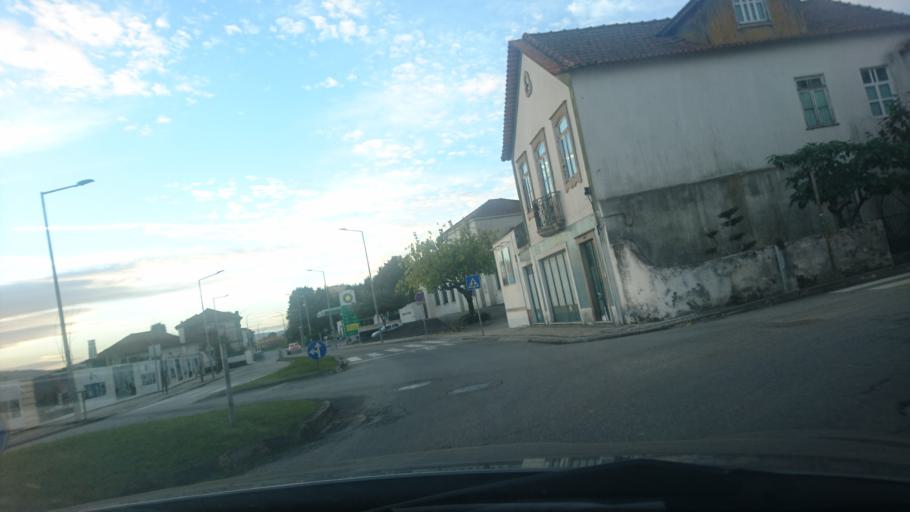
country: PT
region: Aveiro
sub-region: Sao Joao da Madeira
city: Sao Joao da Madeira
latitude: 40.8945
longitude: -8.4906
